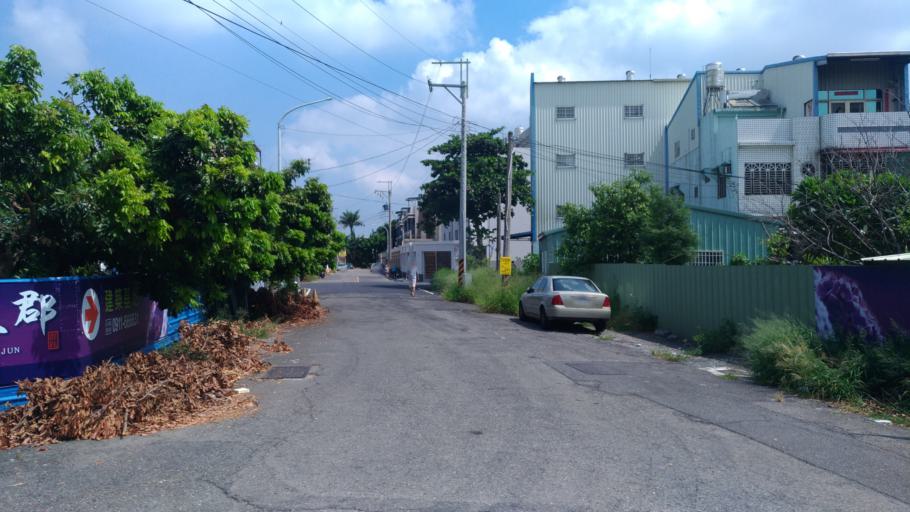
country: TW
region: Taiwan
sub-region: Yunlin
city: Douliu
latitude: 23.7589
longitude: 120.5039
